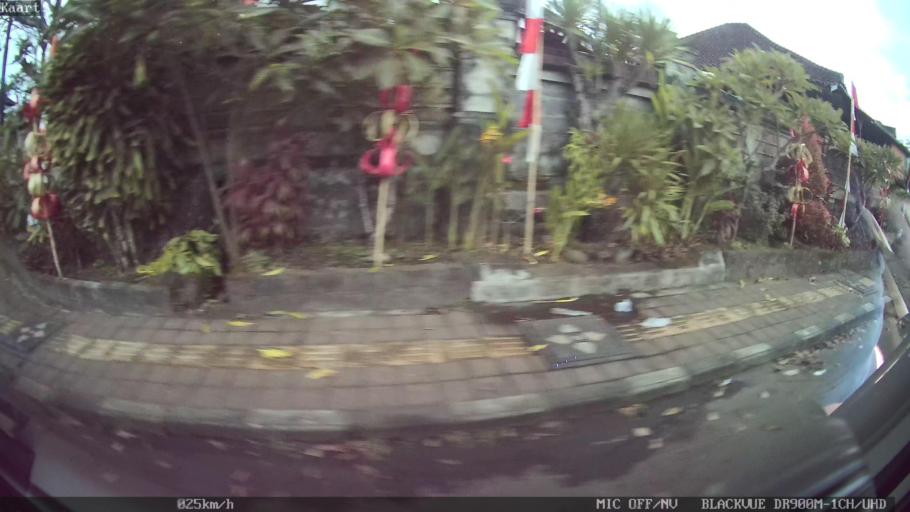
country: ID
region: Bali
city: Banjar Tegal Belodan
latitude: -8.5403
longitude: 115.1188
